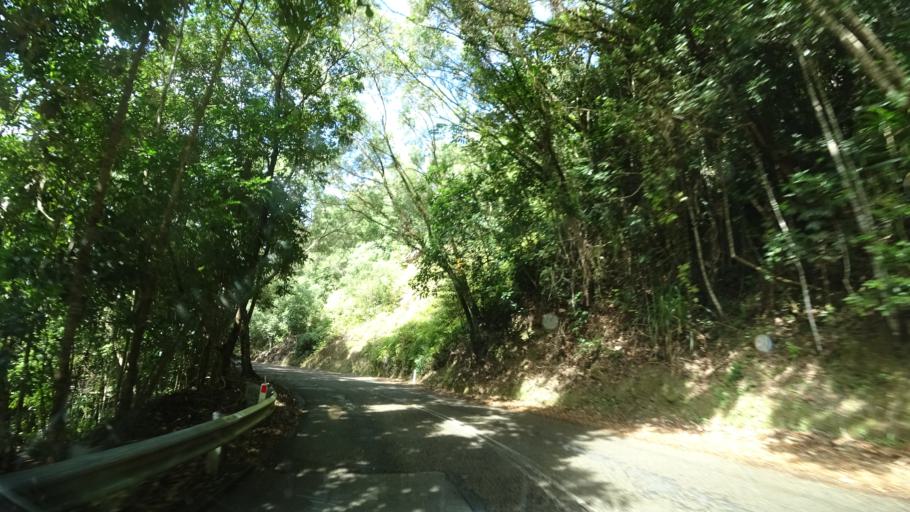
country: AU
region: Queensland
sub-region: Cairns
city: Port Douglas
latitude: -16.2549
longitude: 145.4385
